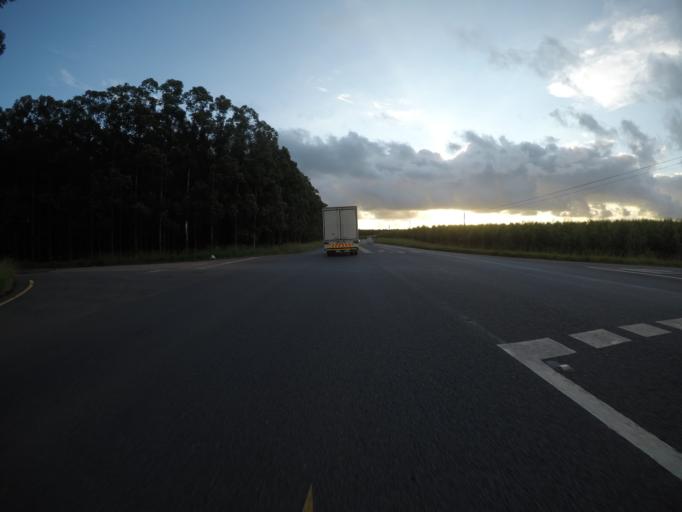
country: ZA
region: KwaZulu-Natal
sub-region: uThungulu District Municipality
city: KwaMbonambi
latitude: -28.5779
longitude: 32.1031
